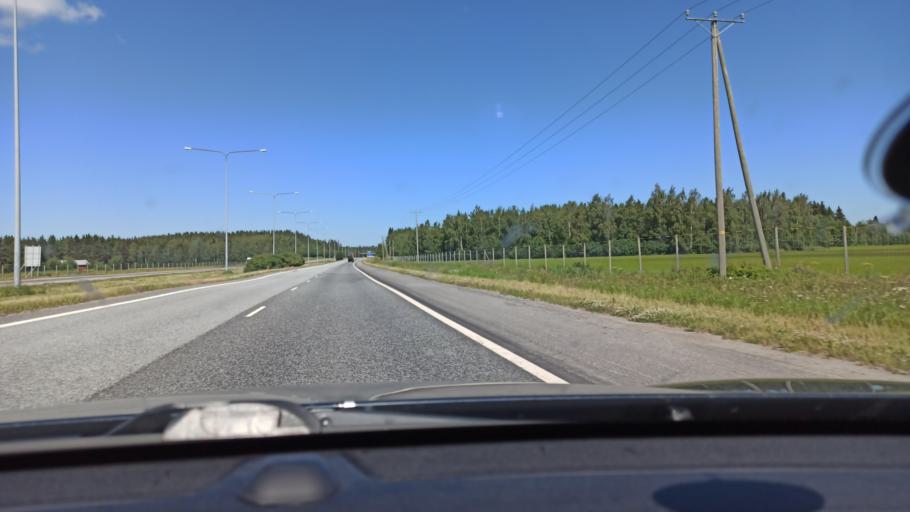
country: FI
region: Ostrobothnia
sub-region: Vaasa
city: Ristinummi
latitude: 63.0456
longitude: 21.7249
